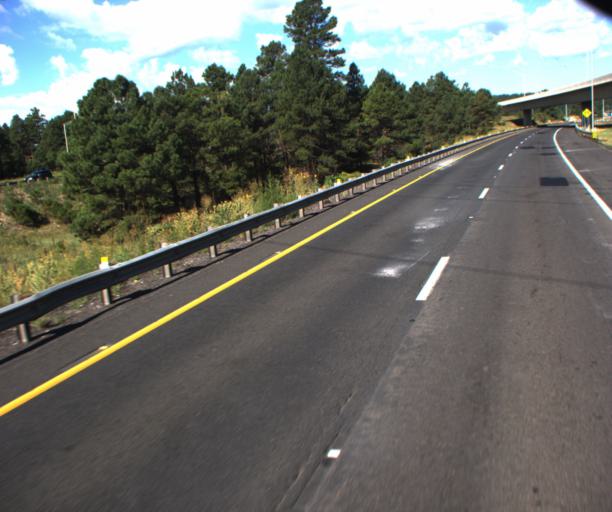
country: US
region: Arizona
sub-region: Coconino County
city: Flagstaff
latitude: 35.1717
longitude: -111.6581
